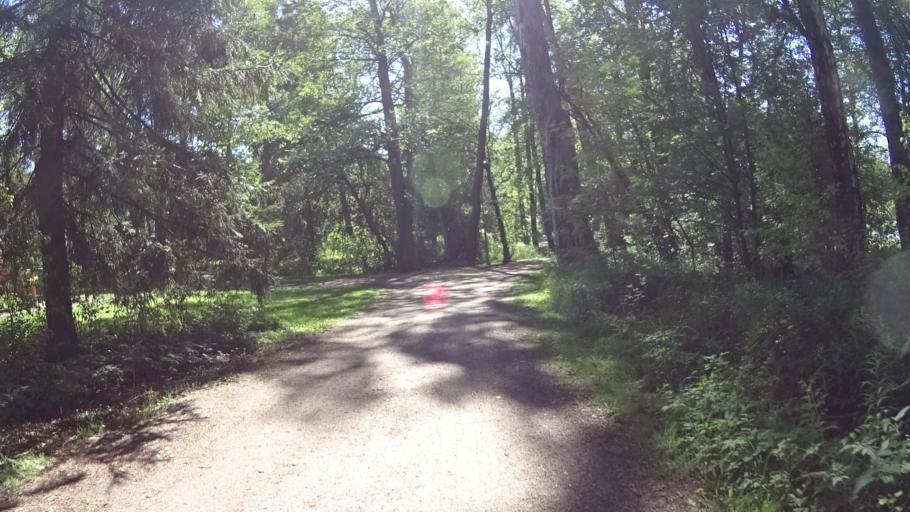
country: FI
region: Uusimaa
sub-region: Helsinki
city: Teekkarikylae
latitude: 60.1795
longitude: 24.8464
